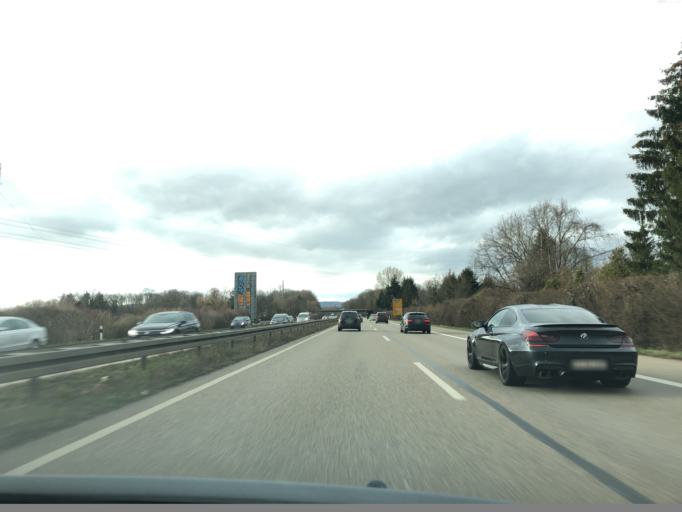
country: DE
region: Baden-Wuerttemberg
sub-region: Freiburg Region
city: Umkirch
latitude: 48.0120
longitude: 7.7982
